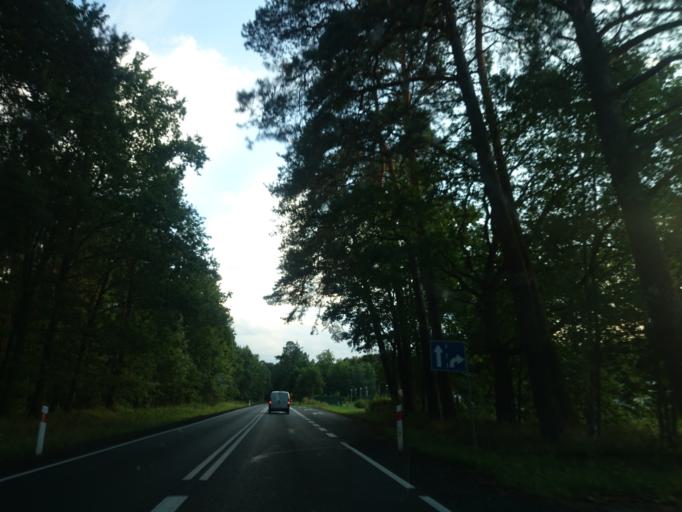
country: PL
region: West Pomeranian Voivodeship
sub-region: Powiat mysliborski
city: Debno
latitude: 52.7705
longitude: 14.7430
